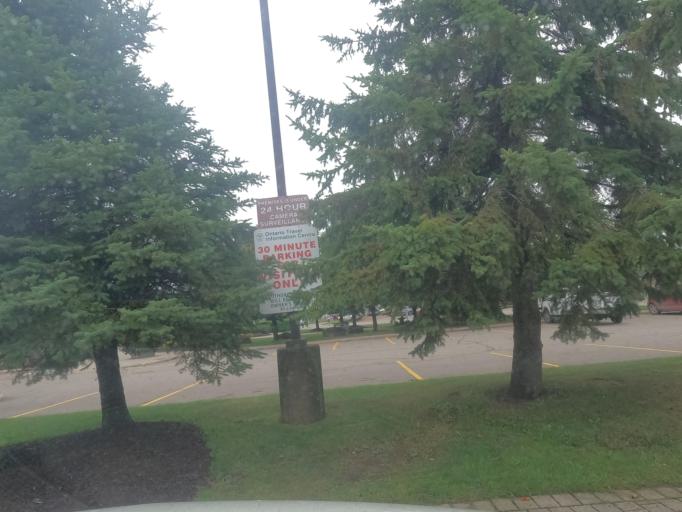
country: CA
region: Ontario
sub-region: Algoma
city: Sault Ste. Marie
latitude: 46.5179
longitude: -84.3468
